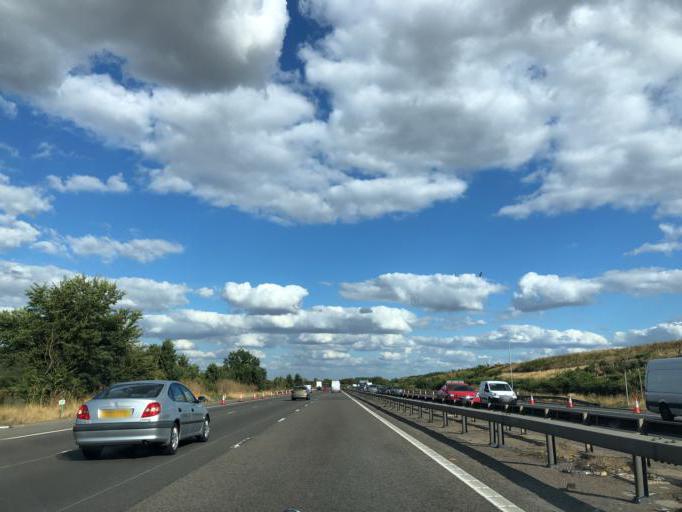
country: GB
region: England
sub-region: Milton Keynes
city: Broughton
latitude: 52.0514
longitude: -0.6780
